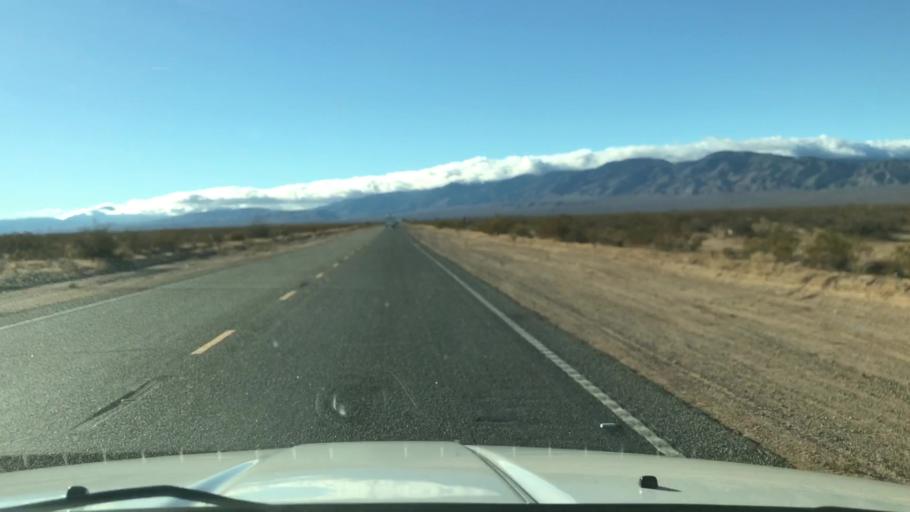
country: US
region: California
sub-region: Kern County
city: California City
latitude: 35.1255
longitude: -118.0519
